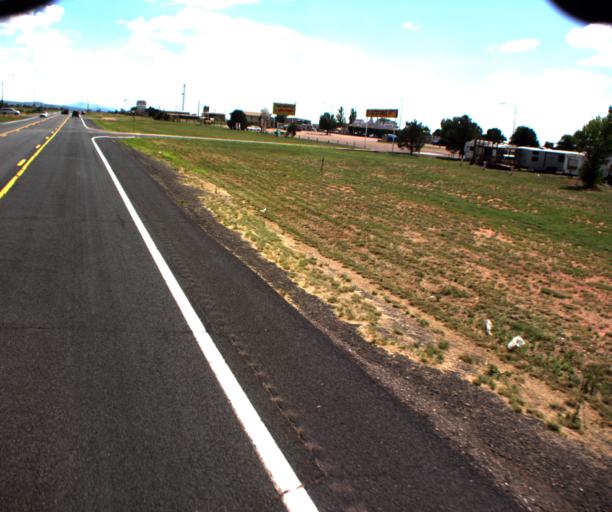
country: US
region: Arizona
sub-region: Coconino County
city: Grand Canyon Village
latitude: 35.6555
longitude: -112.1390
